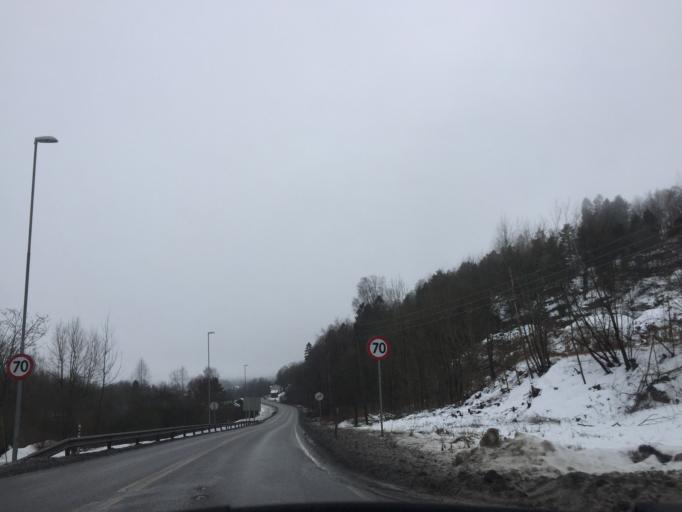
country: NO
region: Akershus
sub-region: Frogn
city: Drobak
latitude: 59.6844
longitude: 10.6679
